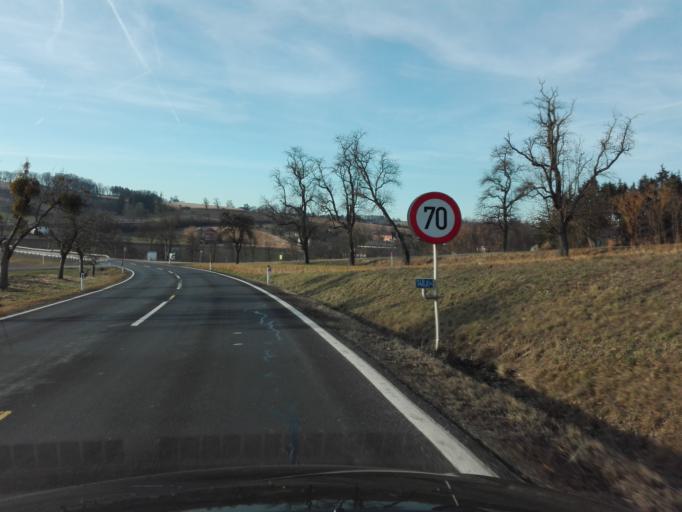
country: AT
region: Lower Austria
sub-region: Politischer Bezirk Amstetten
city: Strengberg
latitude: 48.1395
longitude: 14.6745
